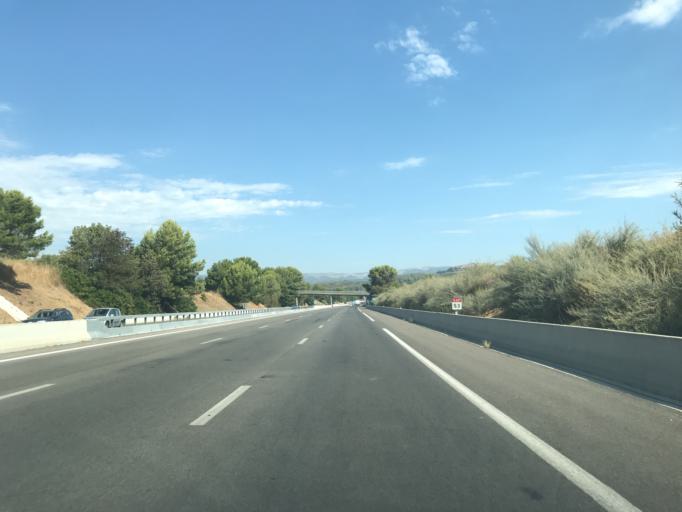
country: FR
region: Provence-Alpes-Cote d'Azur
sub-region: Departement du Var
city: Le Castellet
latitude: 43.1724
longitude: 5.7701
